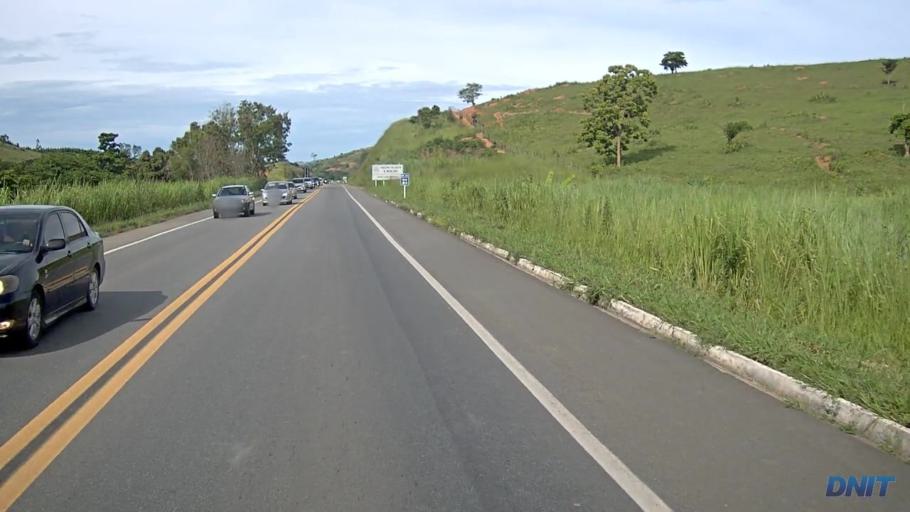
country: BR
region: Minas Gerais
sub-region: Belo Oriente
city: Belo Oriente
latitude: -19.2096
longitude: -42.3039
